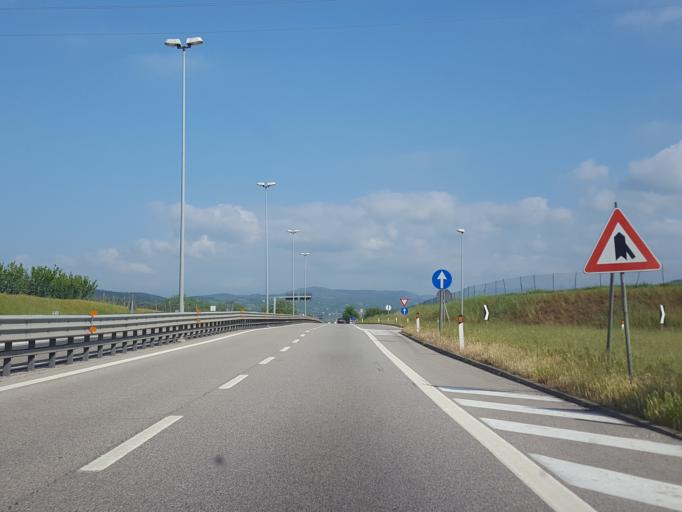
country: IT
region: Veneto
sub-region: Provincia di Verona
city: Montorio
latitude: 45.4410
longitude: 11.0558
